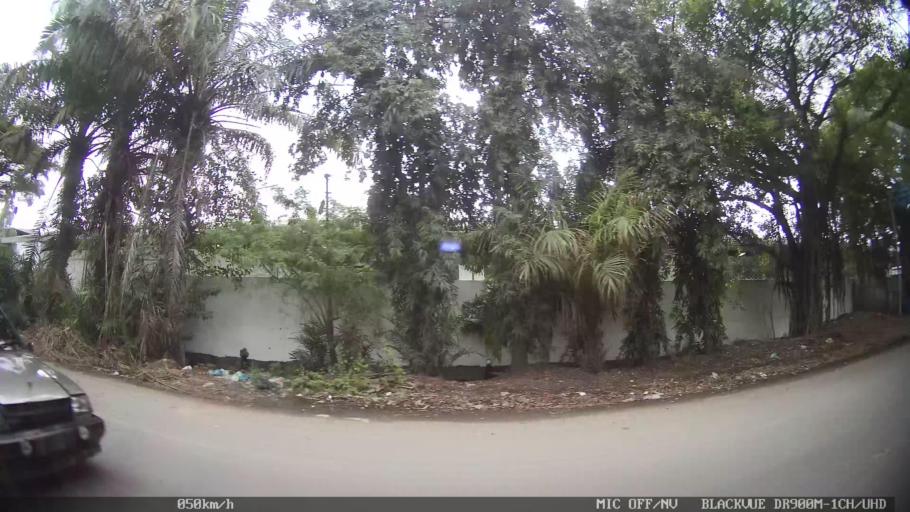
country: ID
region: North Sumatra
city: Labuhan Deli
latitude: 3.6734
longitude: 98.6778
